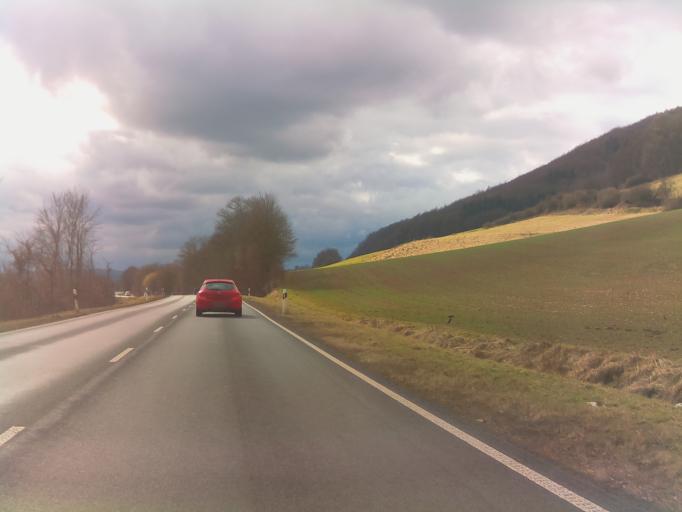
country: DE
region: Hesse
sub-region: Regierungsbezirk Kassel
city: Niederaula
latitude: 50.8195
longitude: 9.6456
